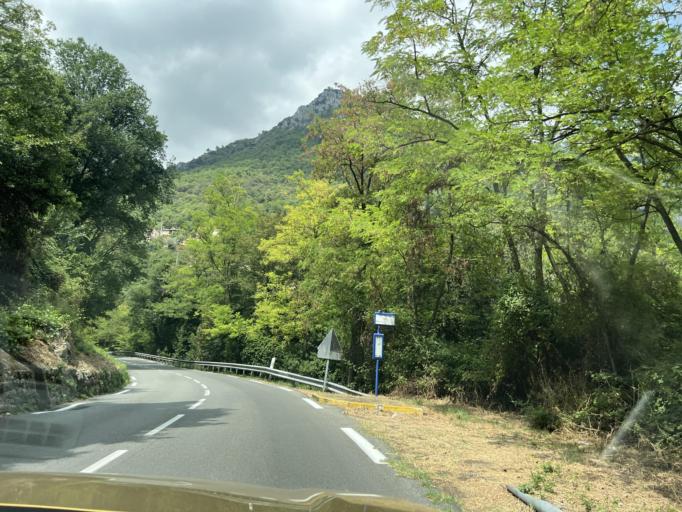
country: FR
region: Provence-Alpes-Cote d'Azur
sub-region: Departement des Alpes-Maritimes
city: Le Rouret
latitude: 43.7121
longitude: 6.9873
